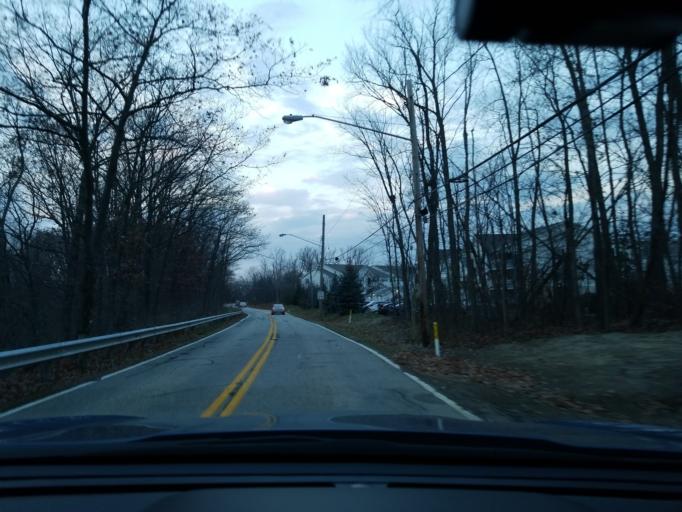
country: US
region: Ohio
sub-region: Cuyahoga County
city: Berea
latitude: 41.3882
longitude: -81.8642
